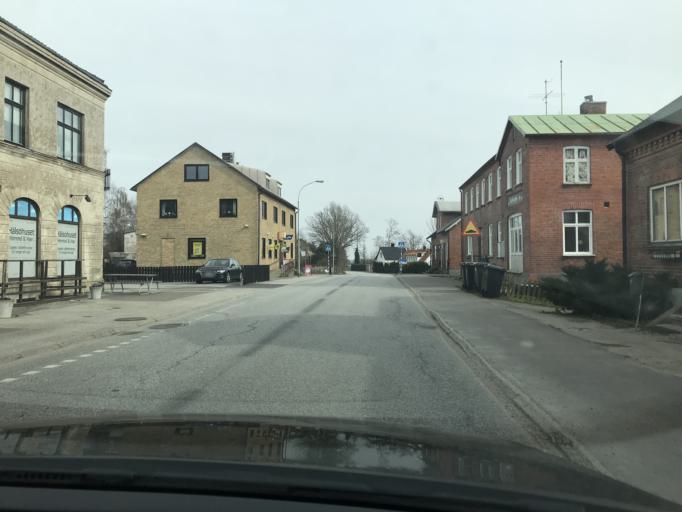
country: SE
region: Skane
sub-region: Skurups Kommun
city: Skivarp
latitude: 55.4231
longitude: 13.5691
